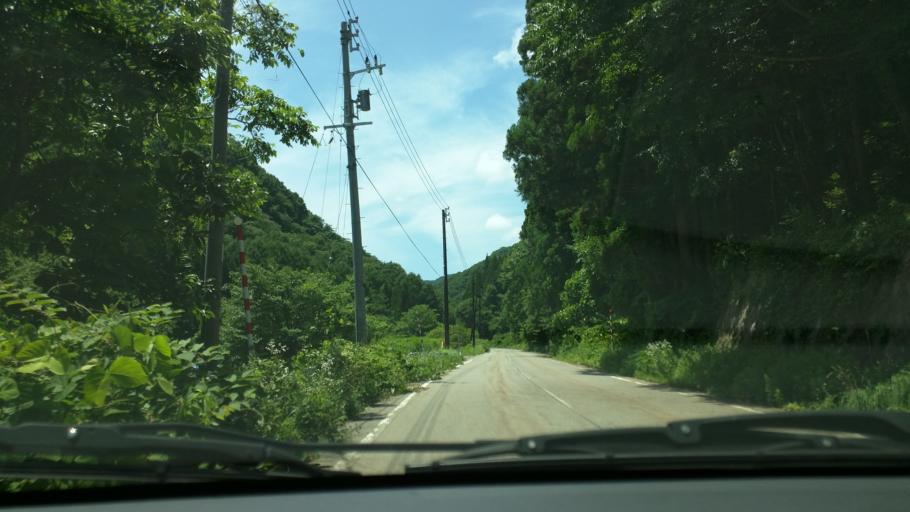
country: JP
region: Fukushima
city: Kitakata
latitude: 37.2578
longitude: 139.7583
